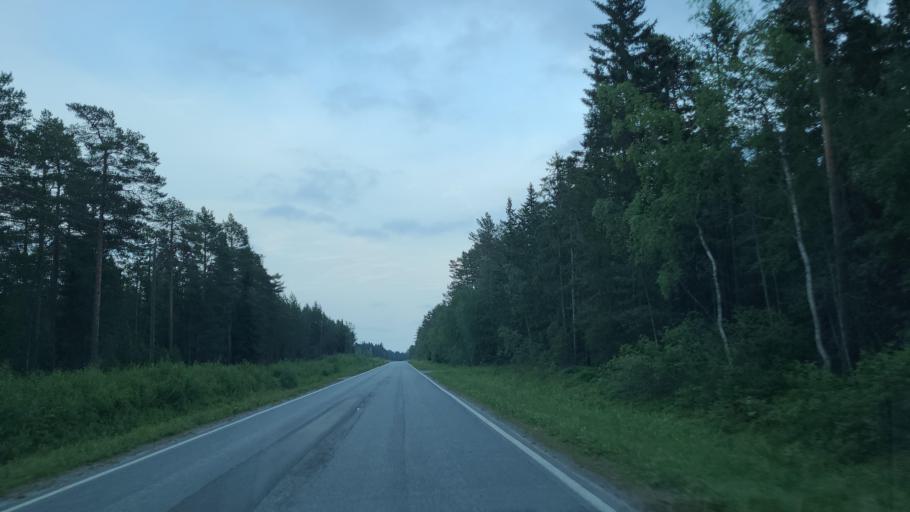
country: FI
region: Ostrobothnia
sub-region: Vaasa
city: Replot
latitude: 63.2029
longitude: 21.2810
